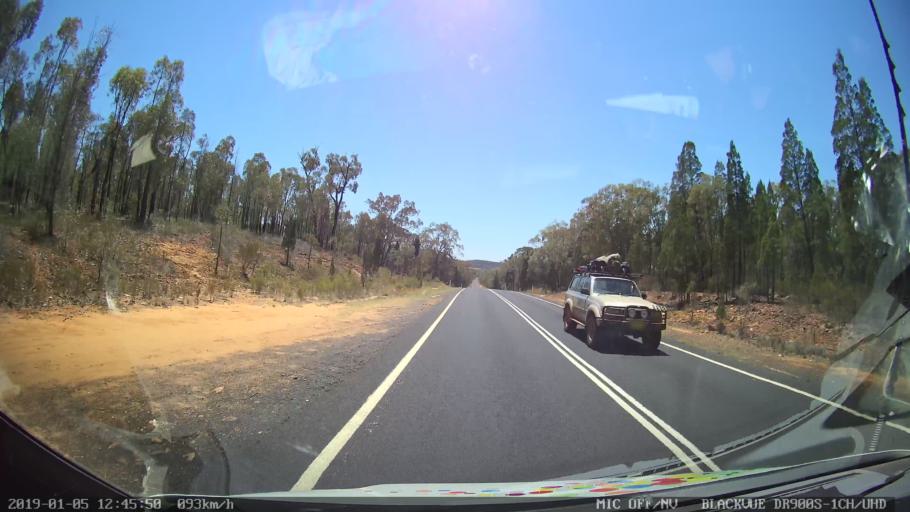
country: AU
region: New South Wales
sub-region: Warrumbungle Shire
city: Coonabarabran
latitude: -31.1239
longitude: 149.5549
